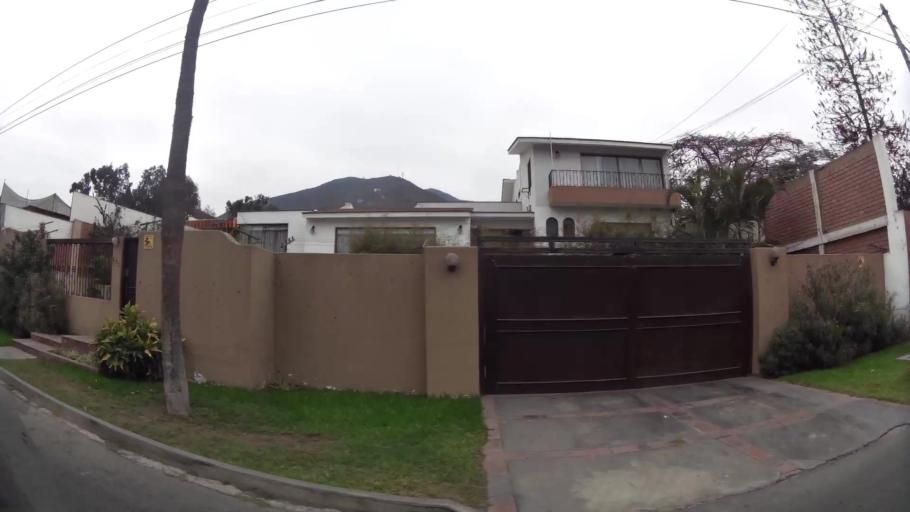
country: PE
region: Lima
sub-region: Lima
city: La Molina
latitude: -12.0802
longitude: -76.9195
